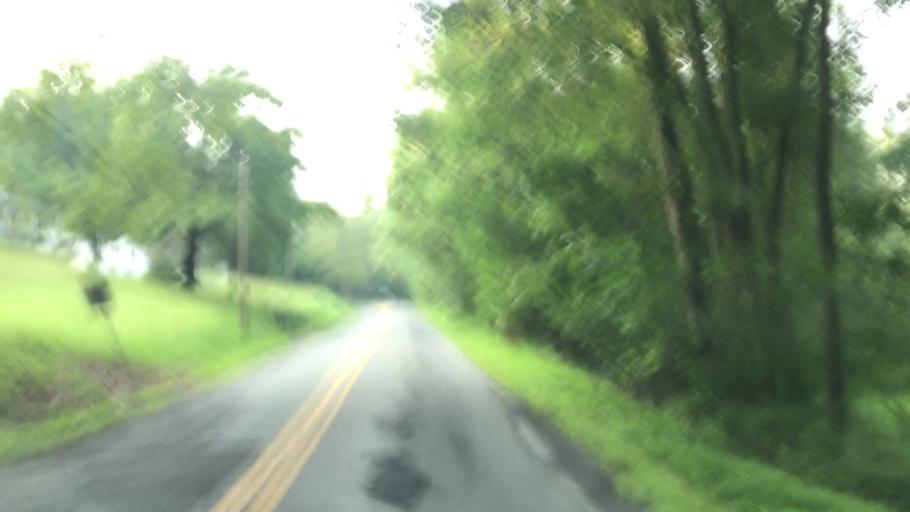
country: US
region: Pennsylvania
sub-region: Wyoming County
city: Factoryville
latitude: 41.6434
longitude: -75.7928
